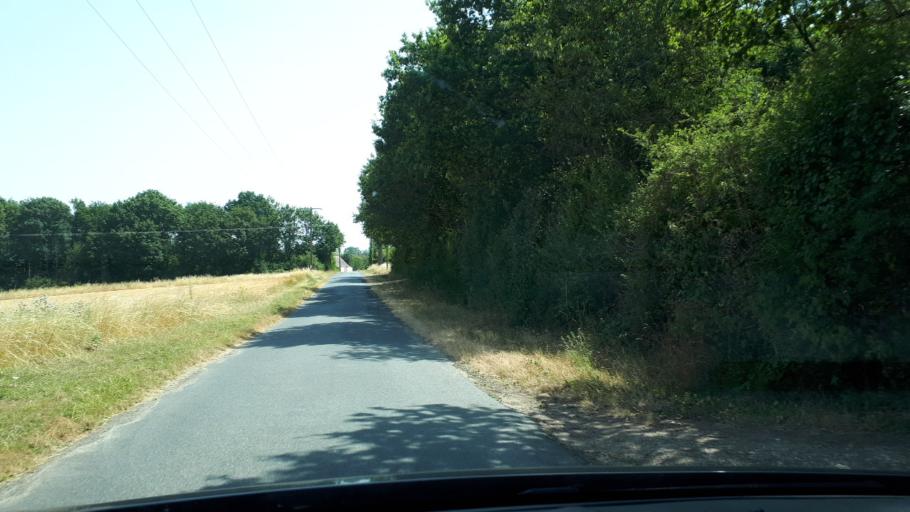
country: FR
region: Centre
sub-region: Departement du Loir-et-Cher
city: Vendome
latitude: 47.8204
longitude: 1.0569
